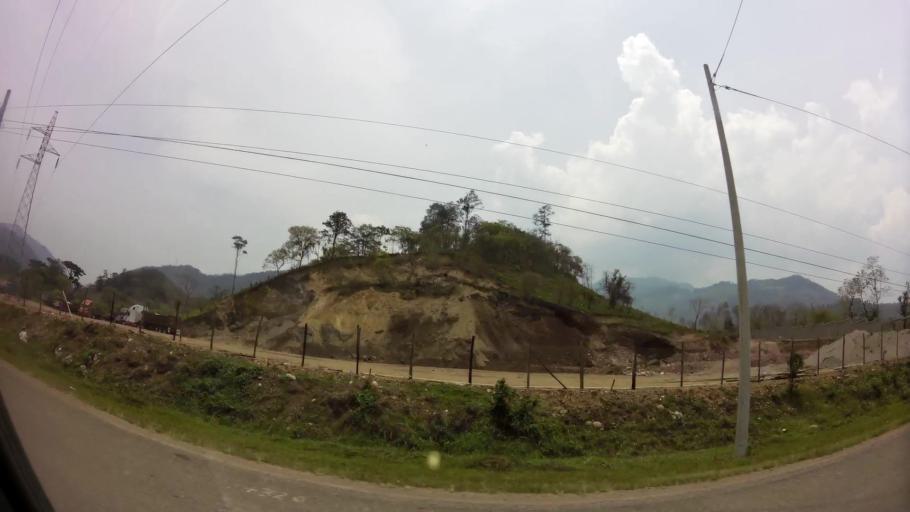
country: HN
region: Comayagua
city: Taulabe
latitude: 14.7117
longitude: -87.9639
